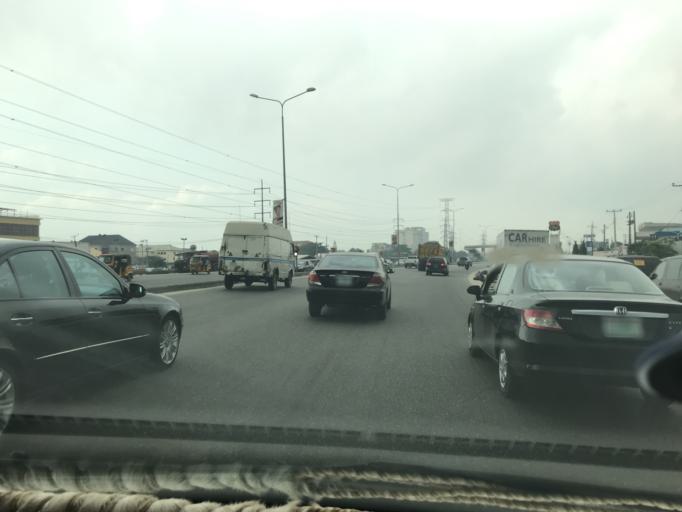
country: NG
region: Lagos
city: Ikoyi
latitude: 6.4511
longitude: 3.5540
